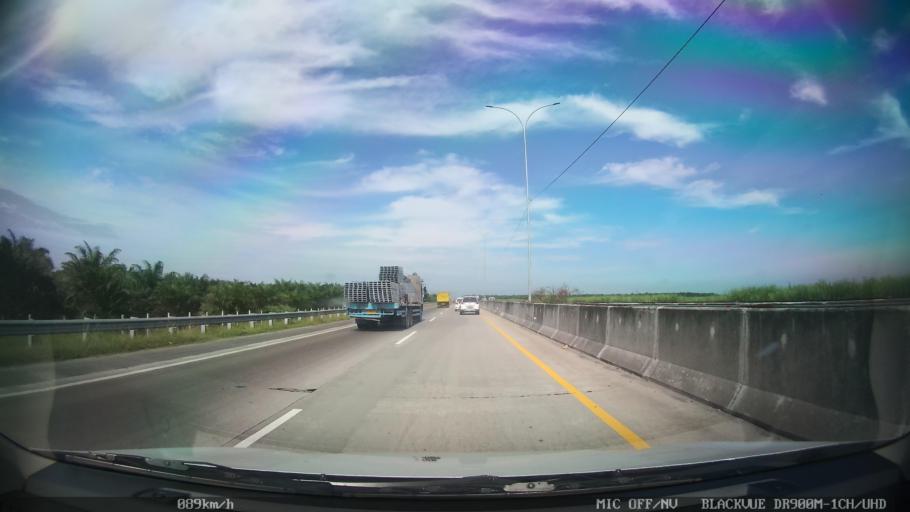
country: ID
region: North Sumatra
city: Sunggal
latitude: 3.6383
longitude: 98.6227
